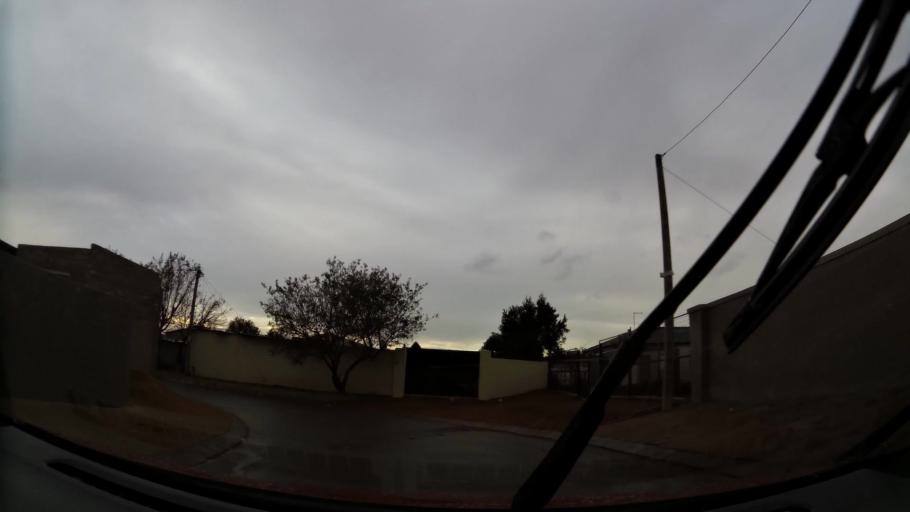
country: ZA
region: Gauteng
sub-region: West Rand District Municipality
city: Randfontein
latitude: -26.1753
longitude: 27.7818
